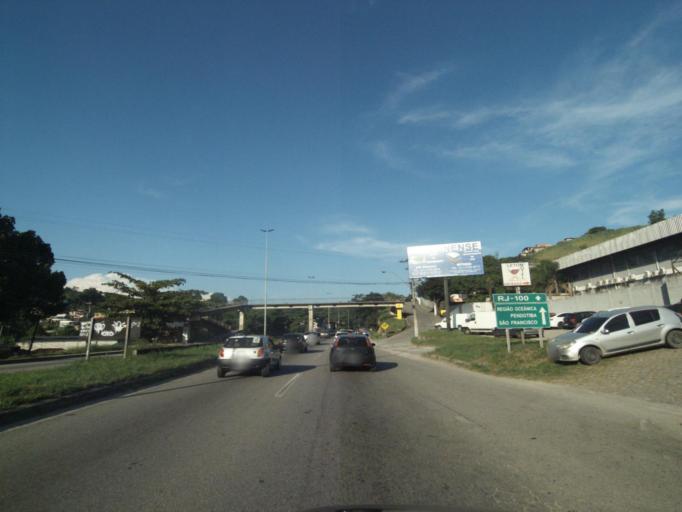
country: BR
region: Rio de Janeiro
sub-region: Niteroi
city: Niteroi
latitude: -22.8826
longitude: -43.0663
